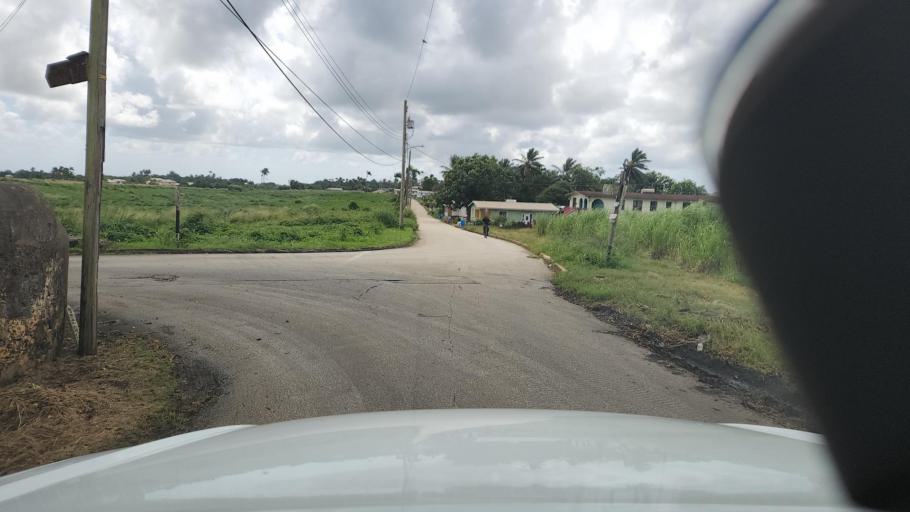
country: BB
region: Saint Joseph
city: Bathsheba
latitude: 13.1943
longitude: -59.5260
